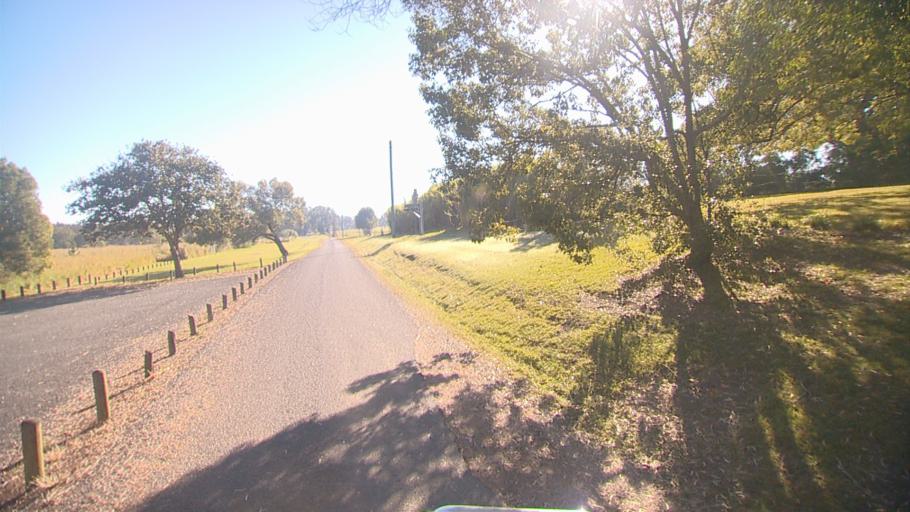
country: AU
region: Queensland
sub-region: Gold Coast
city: Yatala
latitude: -27.6948
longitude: 153.2794
